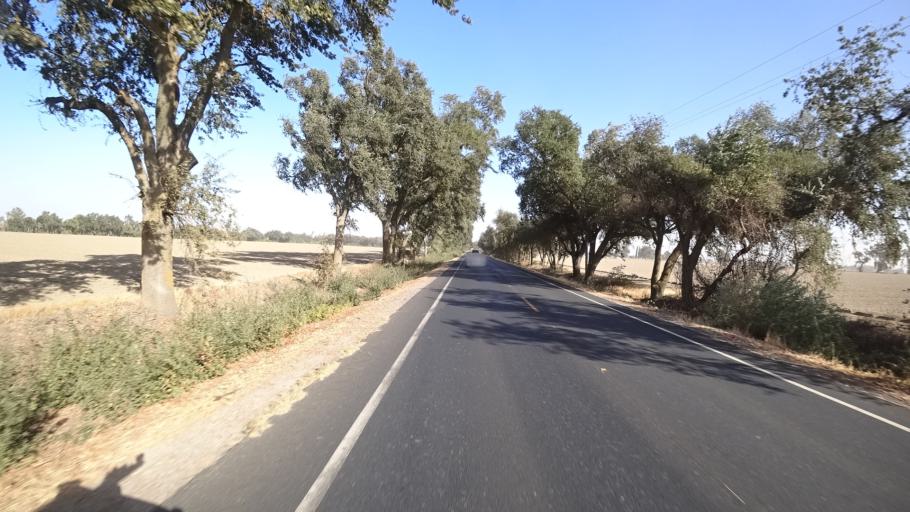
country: US
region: California
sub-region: Yolo County
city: Woodland
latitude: 38.7926
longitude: -121.7353
